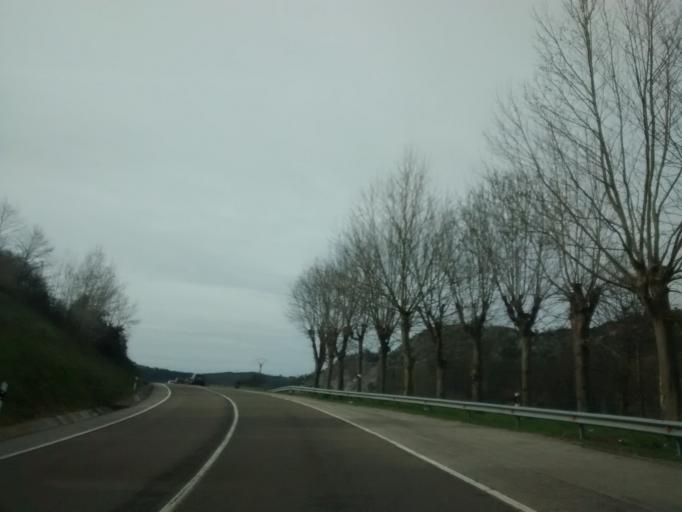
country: ES
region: Cantabria
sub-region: Provincia de Cantabria
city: Corvera
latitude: 43.2806
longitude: -3.9480
